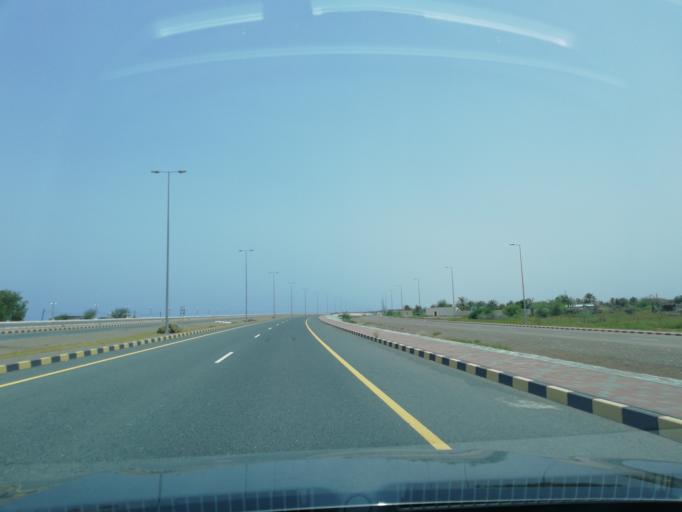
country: OM
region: Al Batinah
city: Shinas
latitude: 24.8264
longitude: 56.4369
